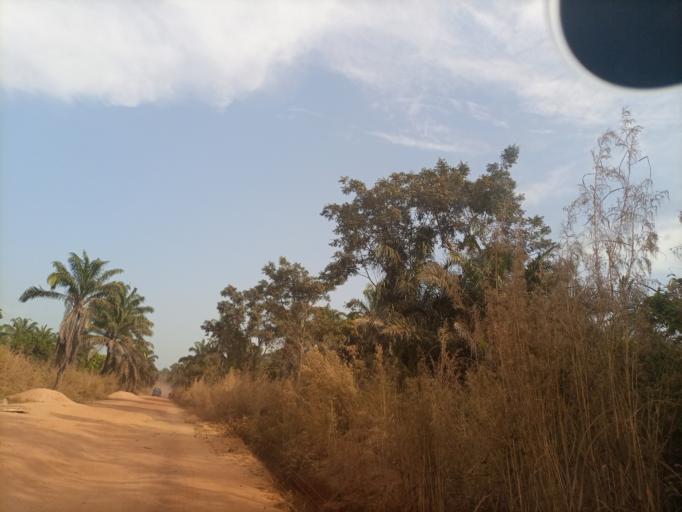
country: NG
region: Enugu
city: Obolo-Eke (1)
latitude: 6.8086
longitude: 7.5551
